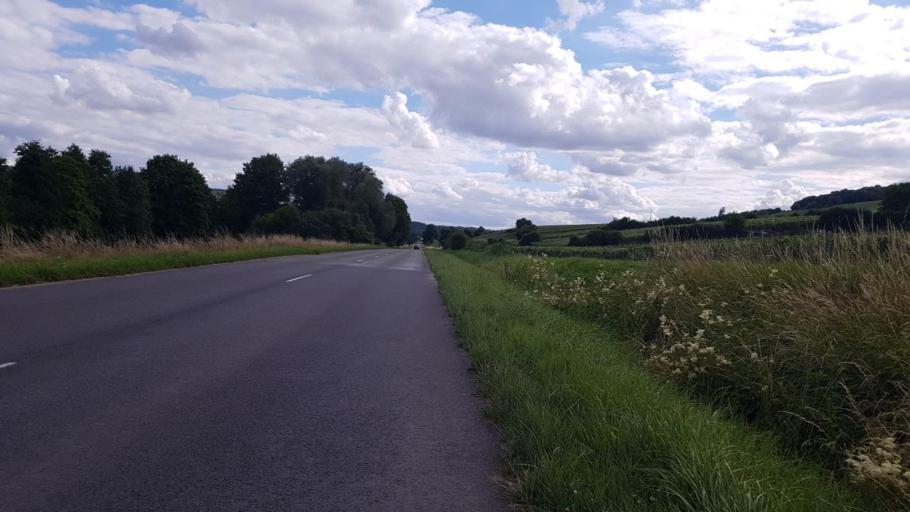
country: FR
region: Picardie
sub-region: Departement de l'Aisne
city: Crezancy
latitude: 49.0628
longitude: 3.4779
